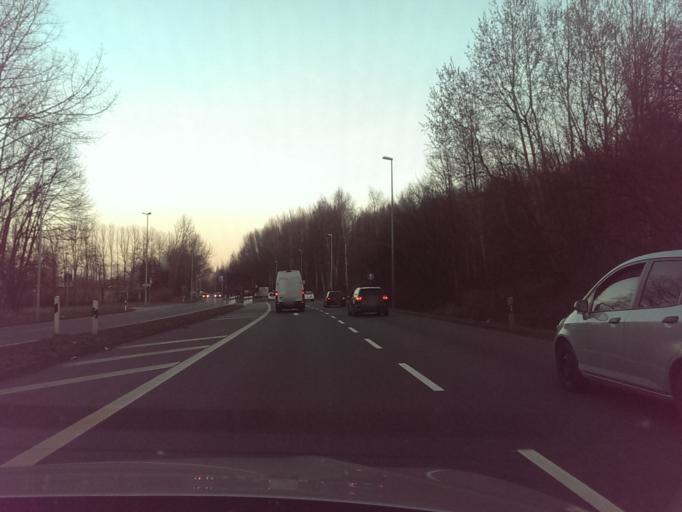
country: DE
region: Saxony
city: Neukirchen
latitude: 50.8060
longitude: 12.8781
